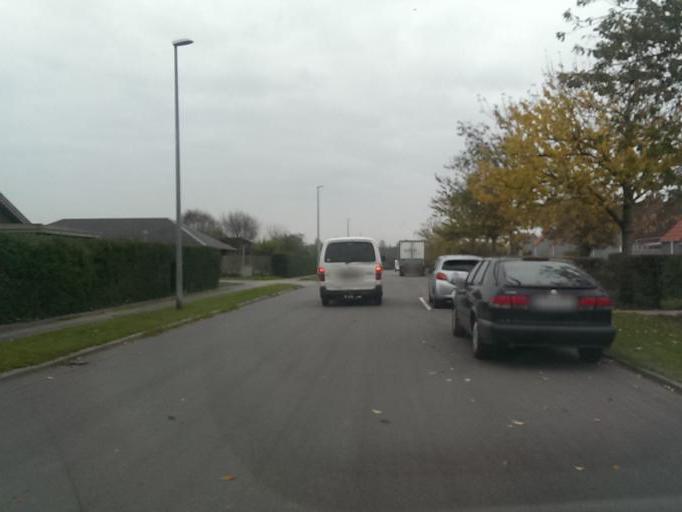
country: DK
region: South Denmark
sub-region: Esbjerg Kommune
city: Esbjerg
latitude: 55.5230
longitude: 8.4441
